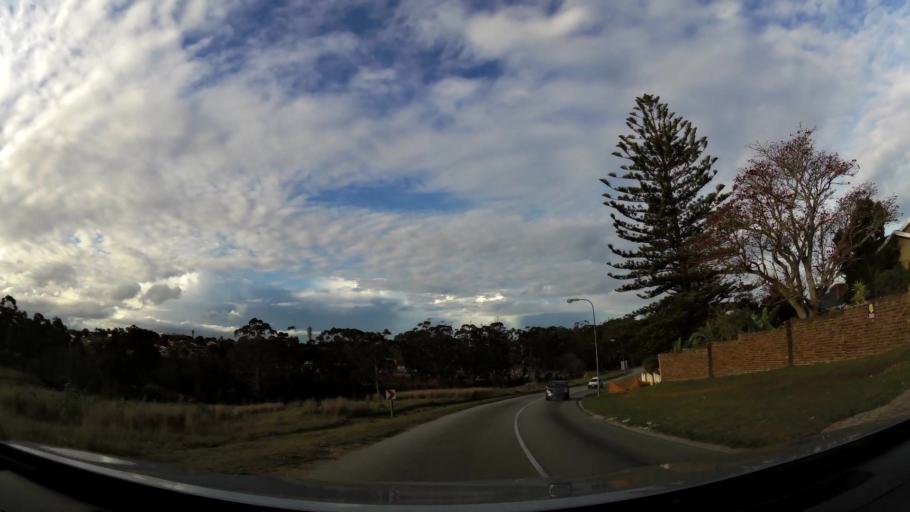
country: ZA
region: Eastern Cape
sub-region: Nelson Mandela Bay Metropolitan Municipality
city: Port Elizabeth
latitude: -33.9545
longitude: 25.5051
